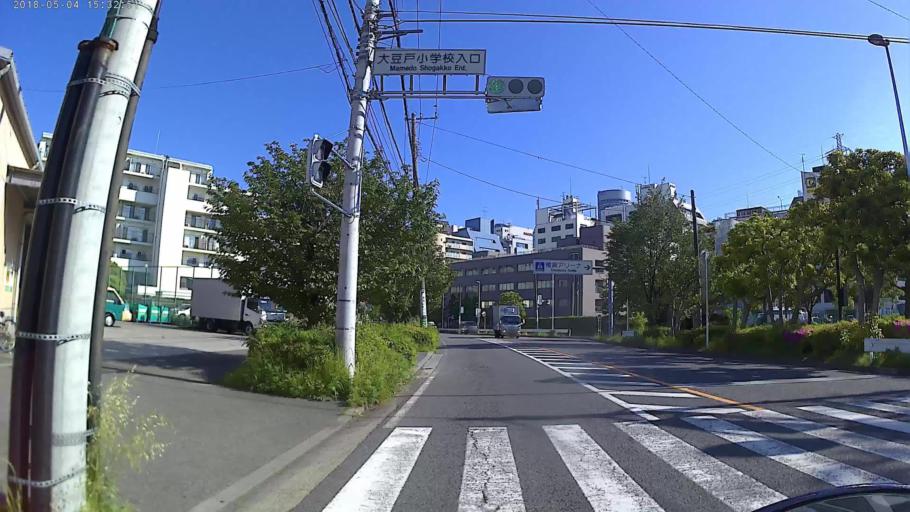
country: JP
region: Kanagawa
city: Yokohama
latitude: 35.5155
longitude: 139.6208
